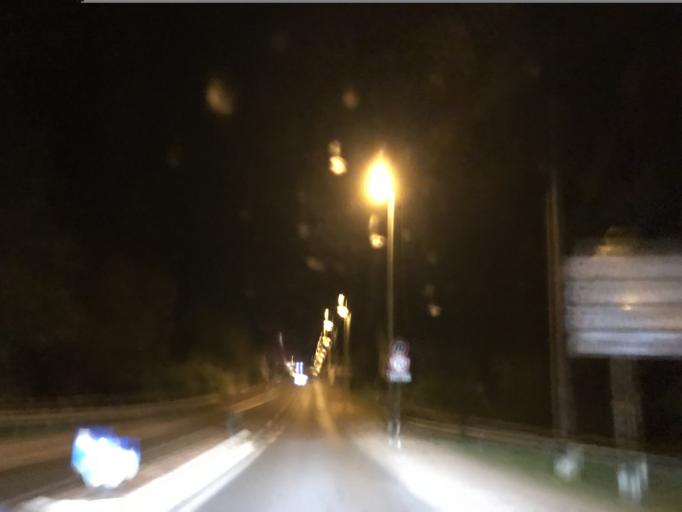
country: FR
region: Auvergne
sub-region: Departement de l'Allier
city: Saint-Yorre
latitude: 46.0744
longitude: 3.4644
